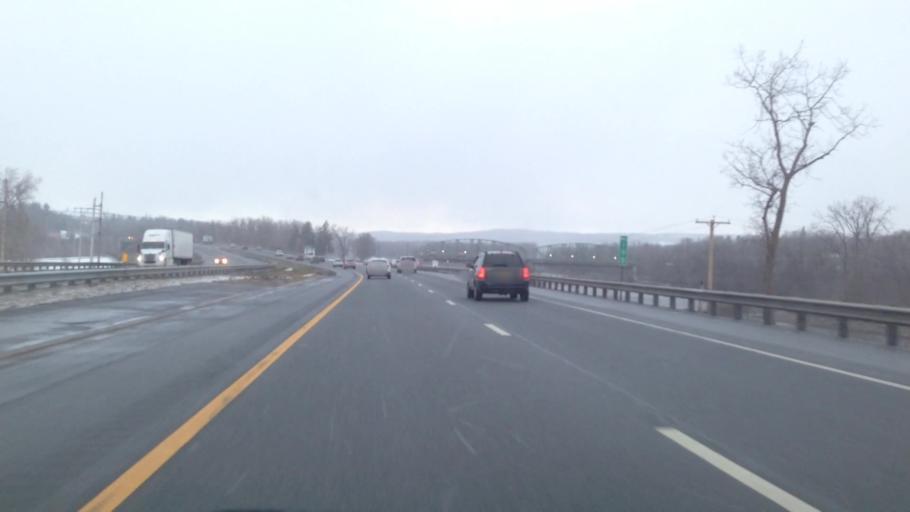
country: US
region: New York
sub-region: Montgomery County
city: Fort Plain
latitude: 42.9338
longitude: -74.6194
